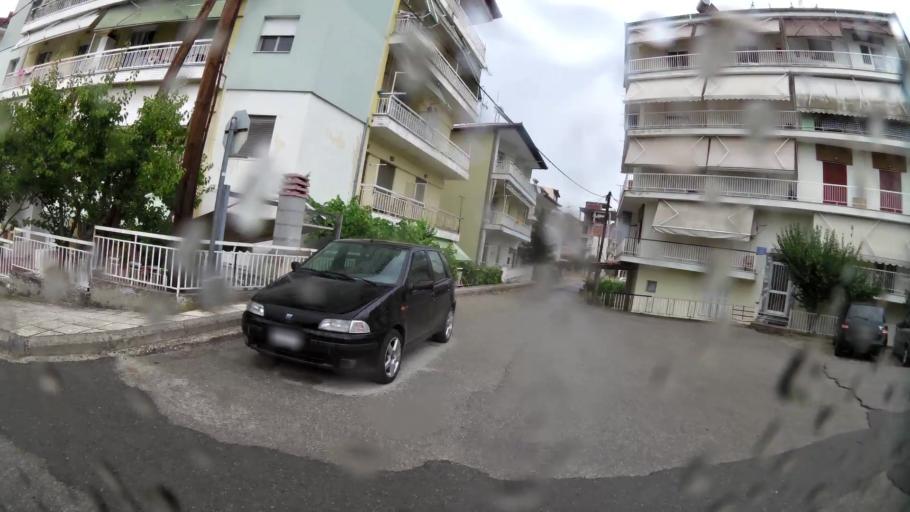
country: GR
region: Central Macedonia
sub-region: Nomos Imathias
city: Veroia
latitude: 40.5268
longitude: 22.1936
